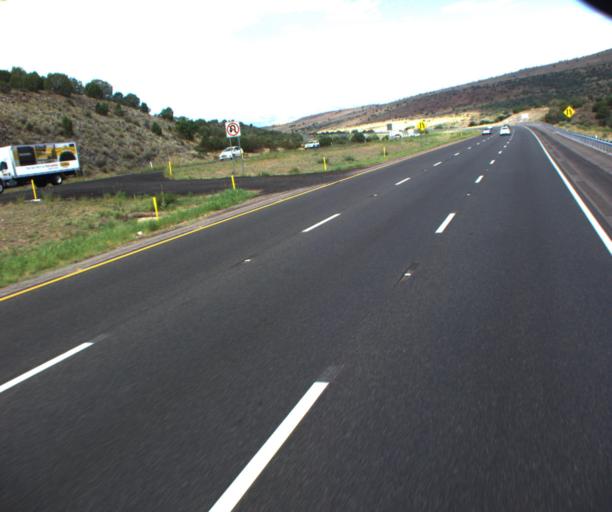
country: US
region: Arizona
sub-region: Yavapai County
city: Camp Verde
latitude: 34.5337
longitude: -111.9687
